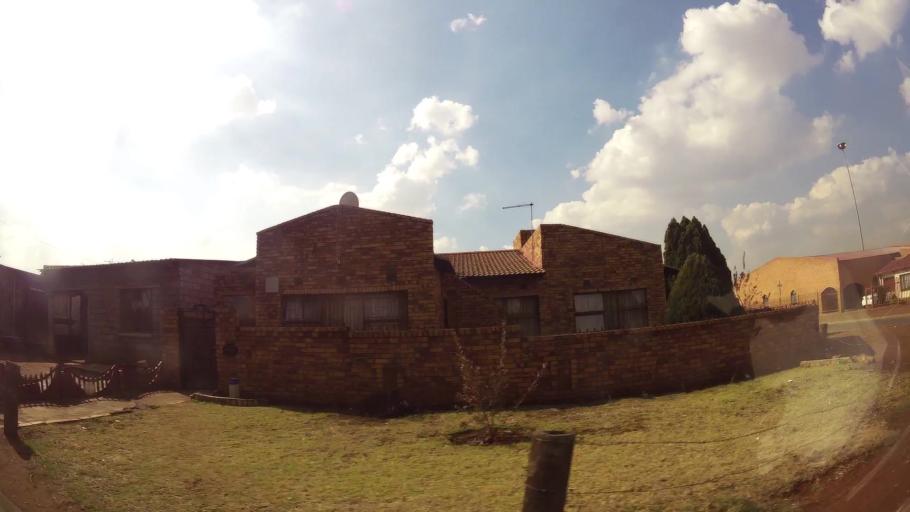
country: ZA
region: Gauteng
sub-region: Ekurhuleni Metropolitan Municipality
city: Germiston
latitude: -26.3483
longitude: 28.1603
